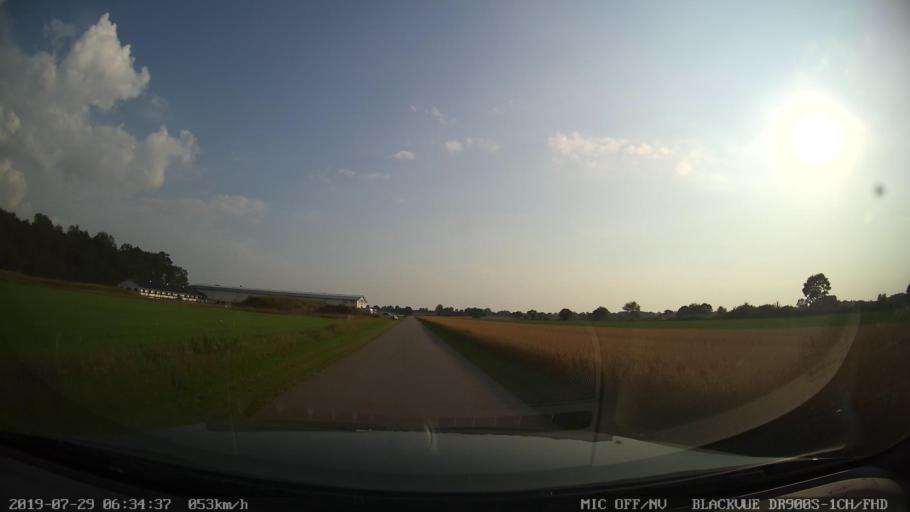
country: SE
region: Skane
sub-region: Helsingborg
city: Odakra
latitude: 56.1188
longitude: 12.7245
